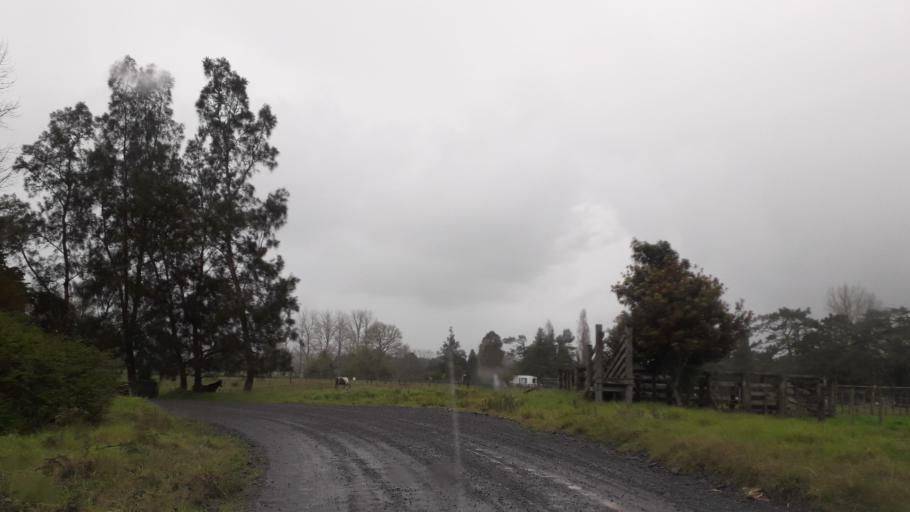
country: NZ
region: Northland
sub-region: Far North District
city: Waimate North
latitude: -35.4721
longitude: 173.6847
